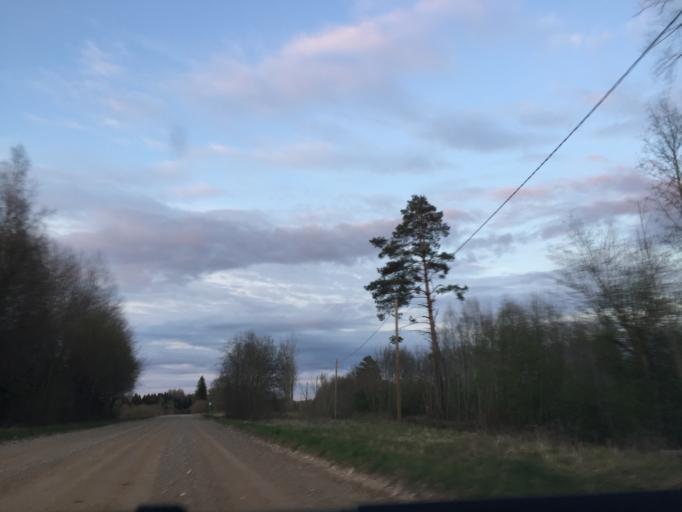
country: LV
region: Aluksnes Rajons
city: Aluksne
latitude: 57.3688
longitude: 27.0058
